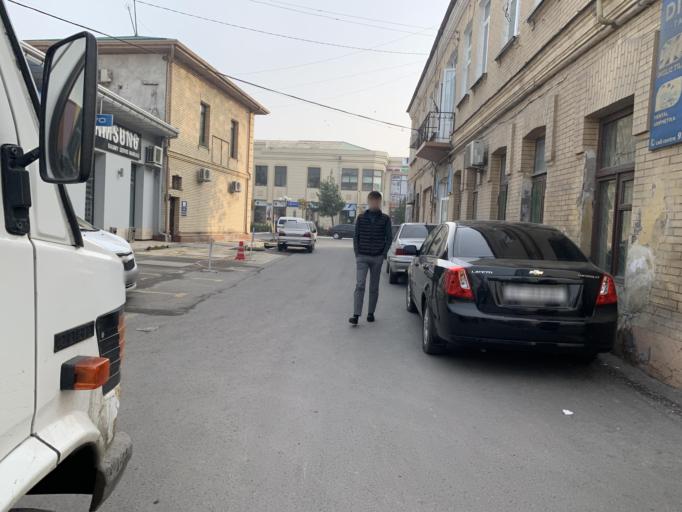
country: UZ
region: Fergana
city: Qo`qon
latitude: 40.5366
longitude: 70.9300
